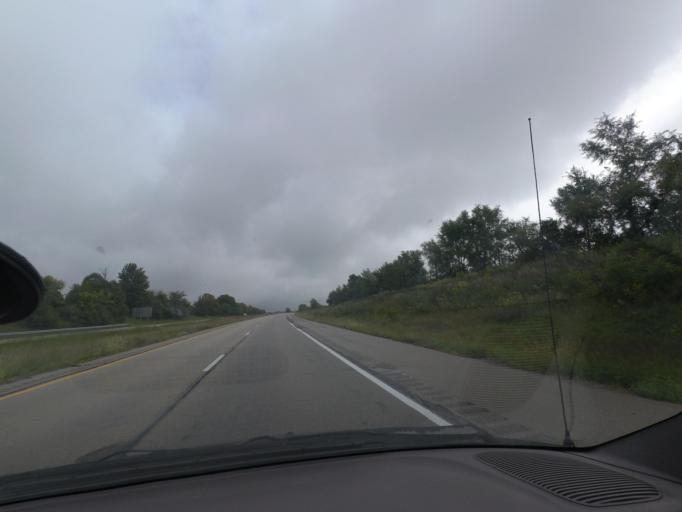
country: US
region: Illinois
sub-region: Piatt County
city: Monticello
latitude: 40.0716
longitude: -88.5416
